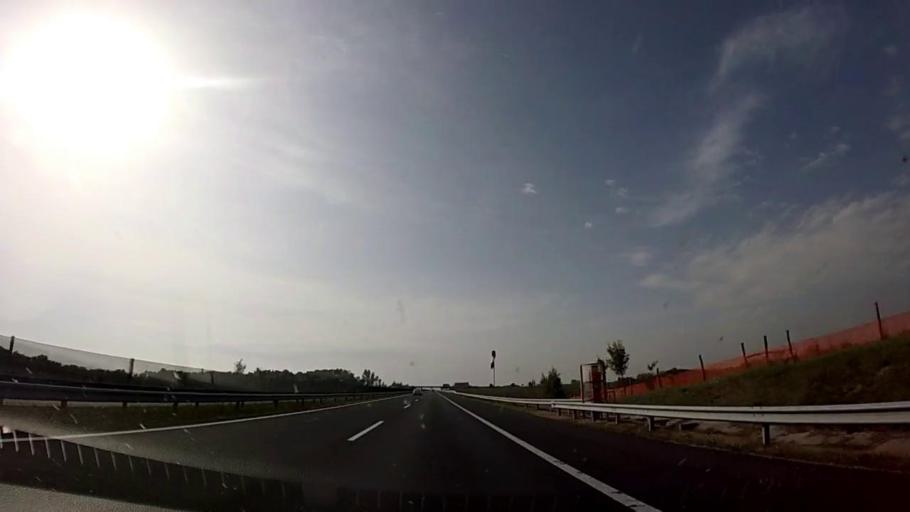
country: HU
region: Zala
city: Nagykanizsa
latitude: 46.4639
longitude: 16.8918
